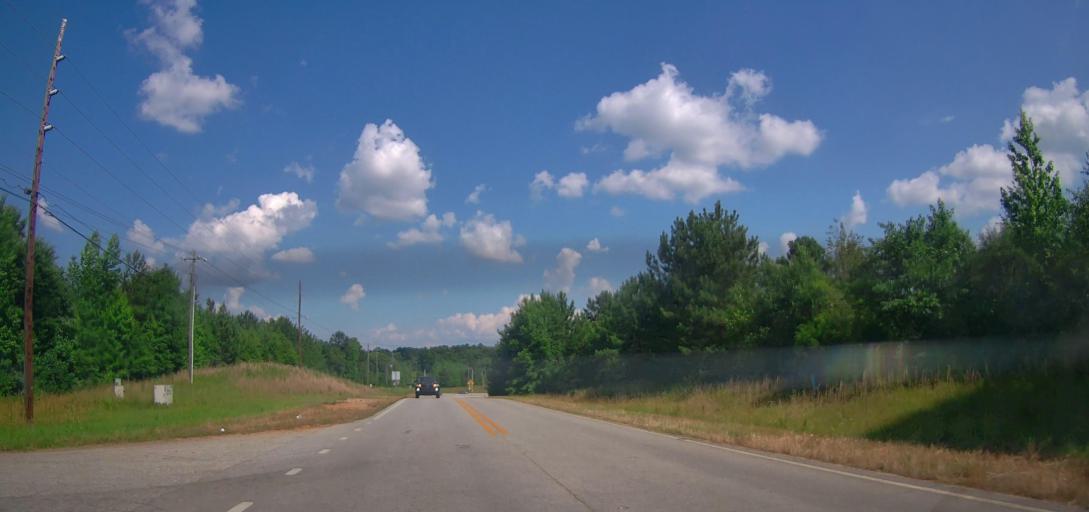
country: US
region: Georgia
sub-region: Spalding County
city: East Griffin
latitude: 33.2419
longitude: -84.1674
